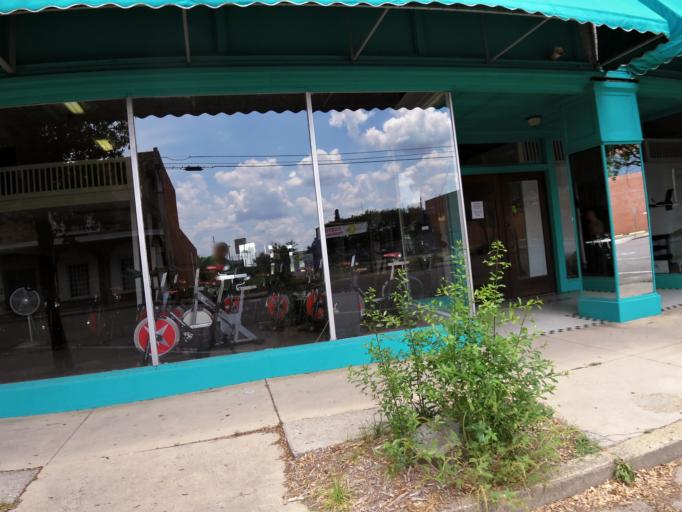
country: US
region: Mississippi
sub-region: Lauderdale County
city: Meridian
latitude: 32.3624
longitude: -88.6998
